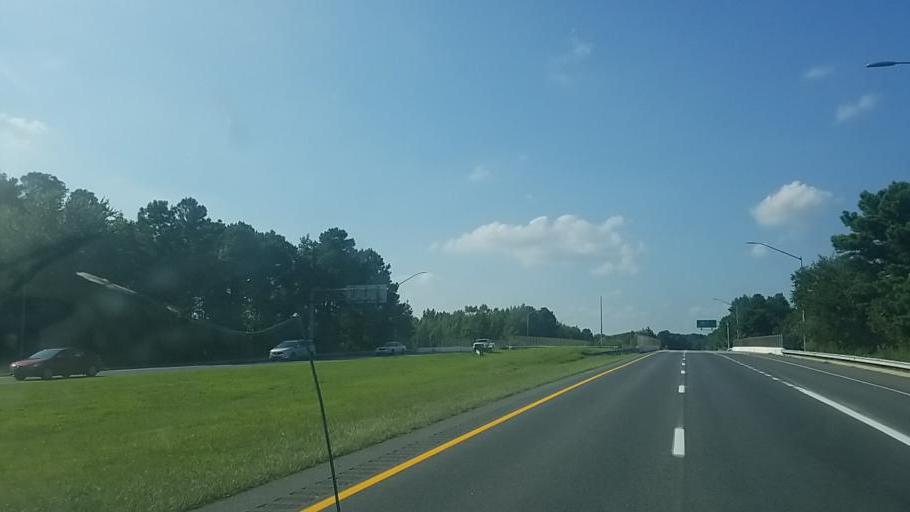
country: US
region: Maryland
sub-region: Worcester County
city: Berlin
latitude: 38.3414
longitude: -75.2131
